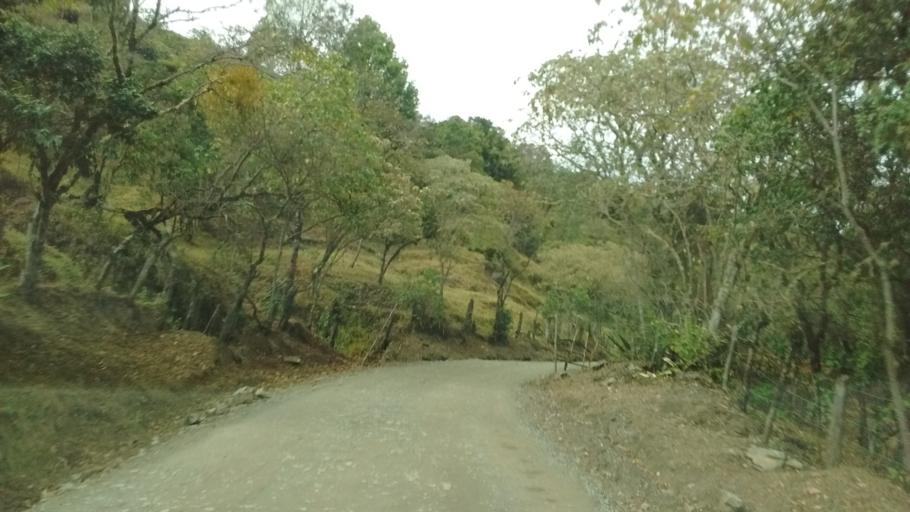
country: CO
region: Cauca
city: Almaguer
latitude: 1.8559
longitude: -76.9458
